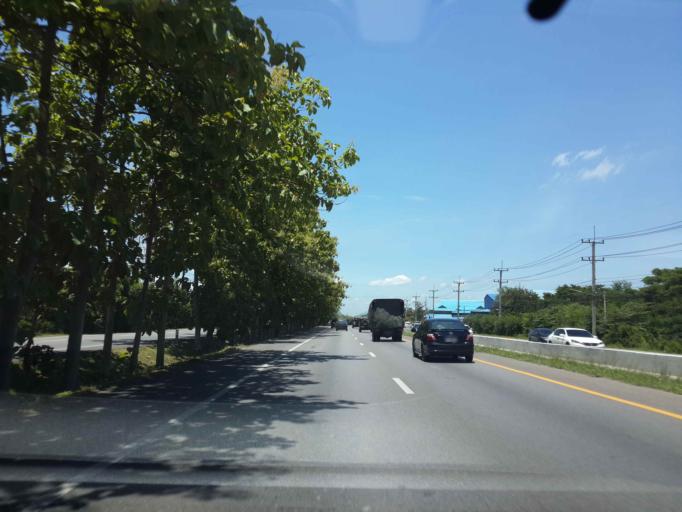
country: TH
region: Phetchaburi
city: Khao Yoi
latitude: 13.1715
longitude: 99.8396
